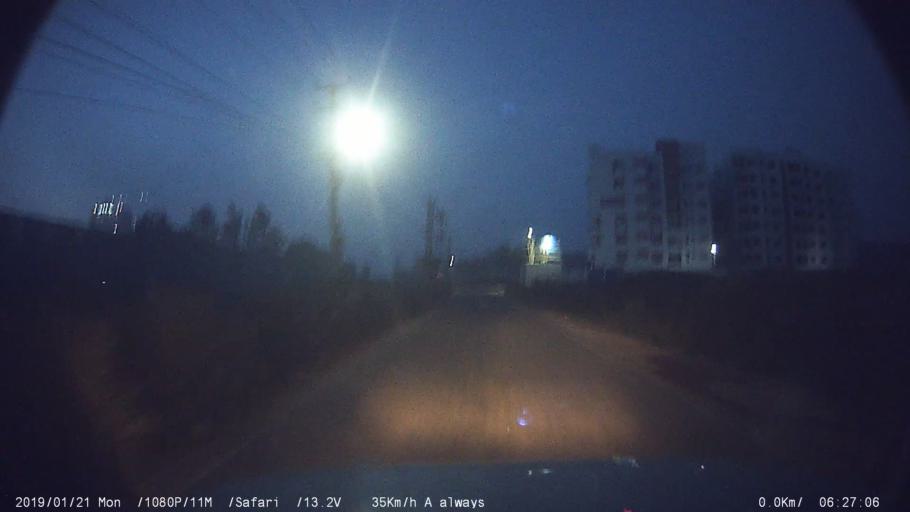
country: IN
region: Karnataka
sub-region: Bangalore Urban
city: Anekal
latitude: 12.8248
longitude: 77.6542
